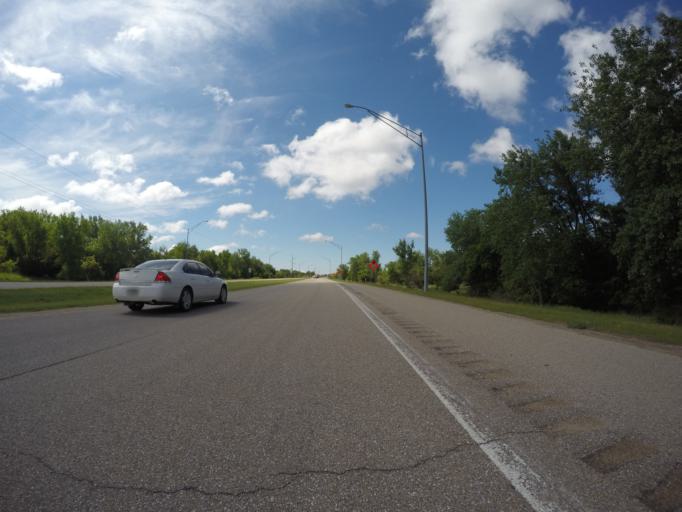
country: US
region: Nebraska
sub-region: Buffalo County
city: Kearney
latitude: 40.6618
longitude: -99.0863
